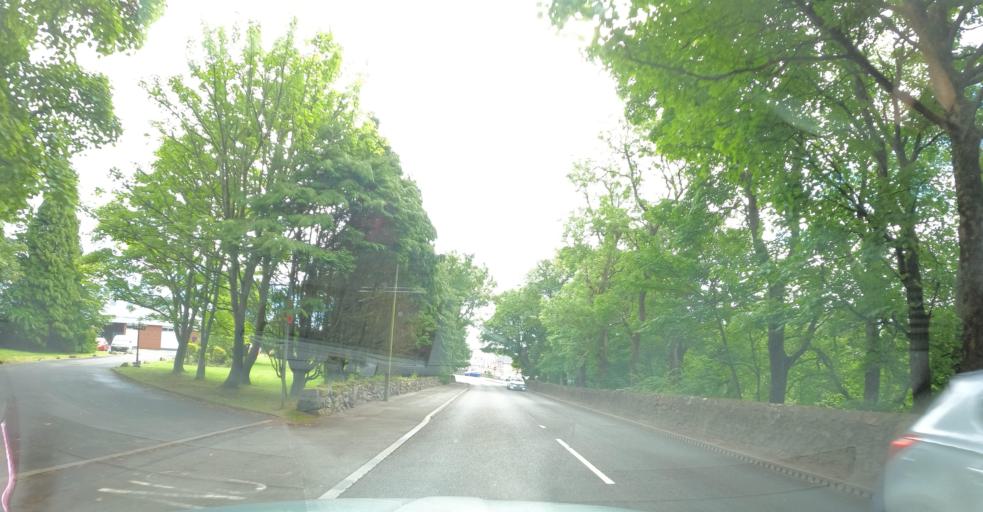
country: GB
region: Scotland
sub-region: Eilean Siar
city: Isle of Lewis
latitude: 58.2191
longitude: -6.3898
